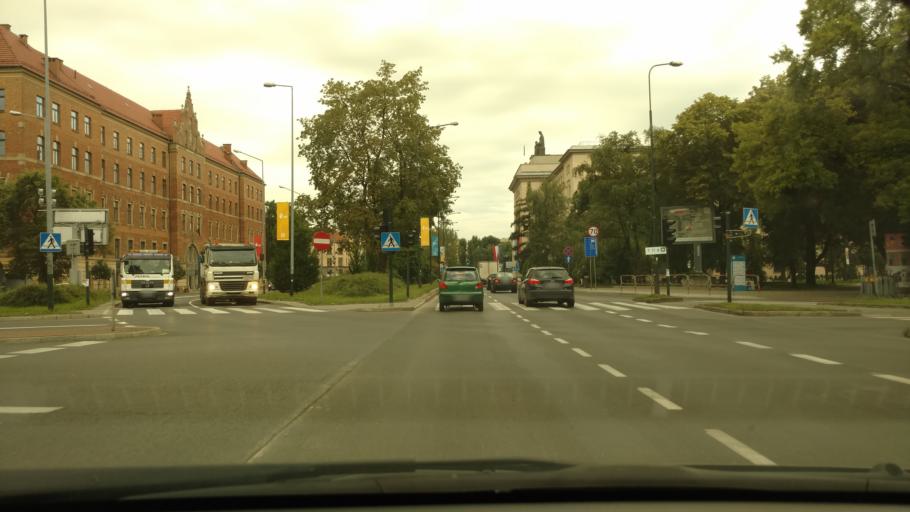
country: PL
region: Lesser Poland Voivodeship
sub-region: Krakow
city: Krakow
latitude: 50.0662
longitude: 19.9245
